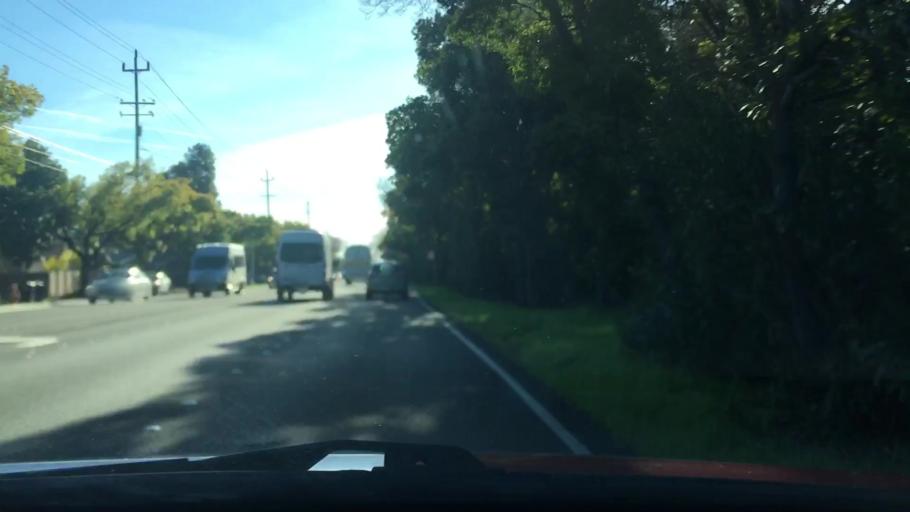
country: US
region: California
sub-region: Santa Clara County
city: Palo Alto
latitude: 37.4220
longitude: -122.1299
